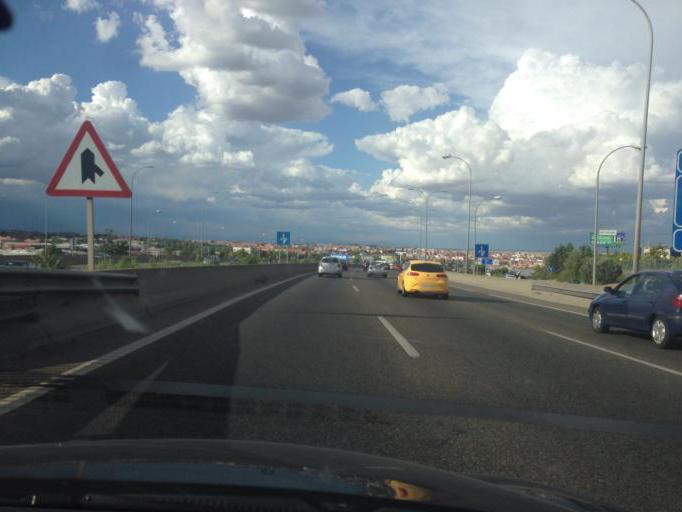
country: ES
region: Madrid
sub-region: Provincia de Madrid
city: Alcobendas
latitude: 40.5267
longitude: -3.6481
